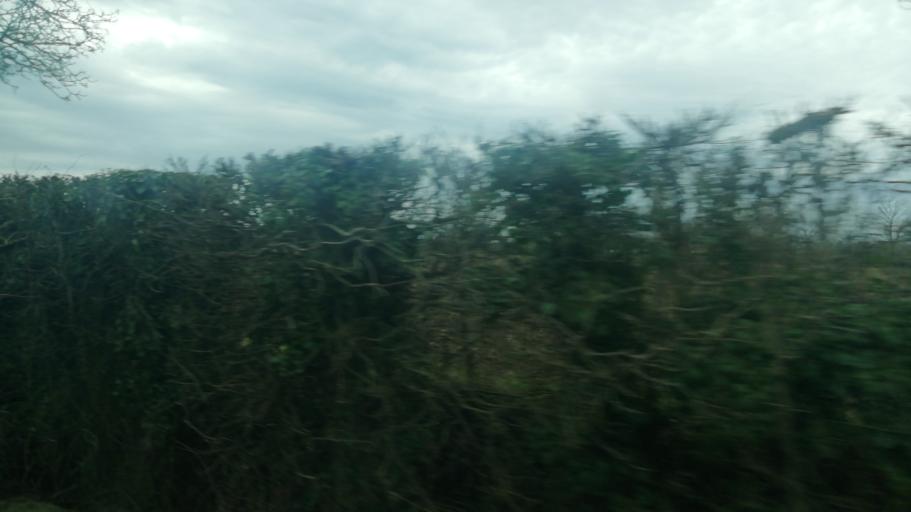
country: IE
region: Leinster
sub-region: Kildare
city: Kilcock
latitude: 53.3536
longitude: -6.6420
